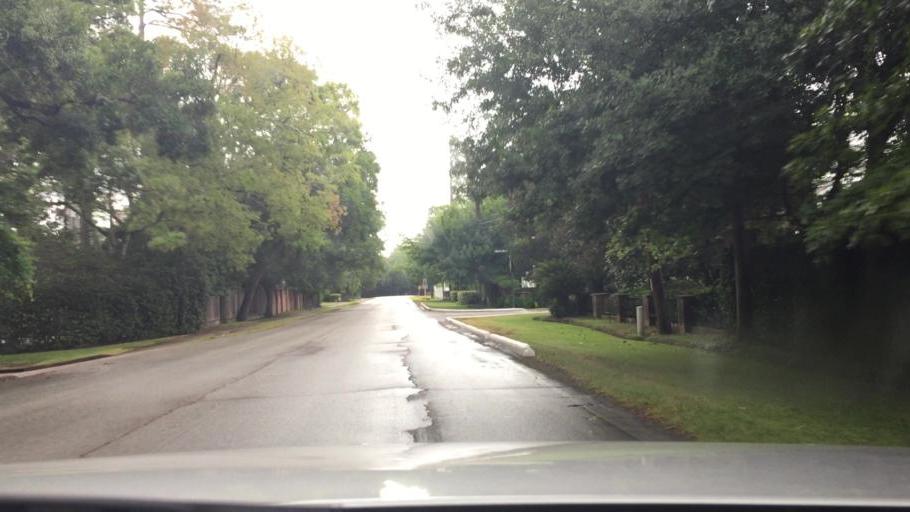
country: US
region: Texas
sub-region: Harris County
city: Hedwig Village
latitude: 29.7734
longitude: -95.5206
